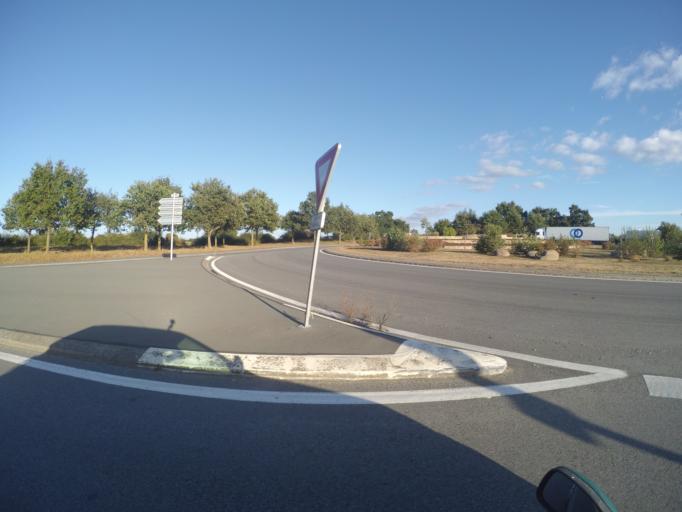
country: FR
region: Pays de la Loire
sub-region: Departement de la Vendee
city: Saint-Hilaire-de-Loulay
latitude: 47.0097
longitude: -1.3384
